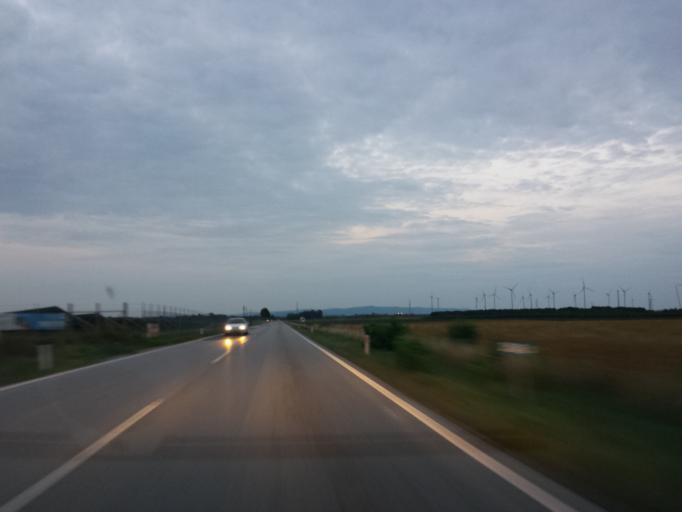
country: AT
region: Lower Austria
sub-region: Politischer Bezirk Baden
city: Oberwaltersdorf
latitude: 47.9703
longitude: 16.3351
